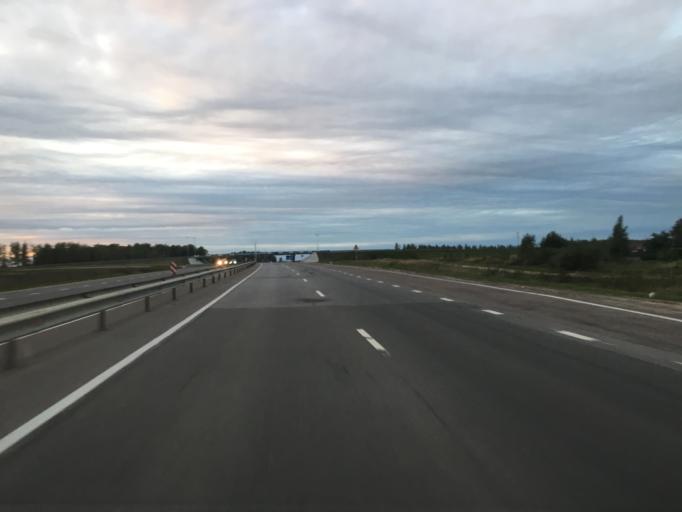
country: RU
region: Kaluga
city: Kaluga
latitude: 54.6217
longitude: 36.2927
